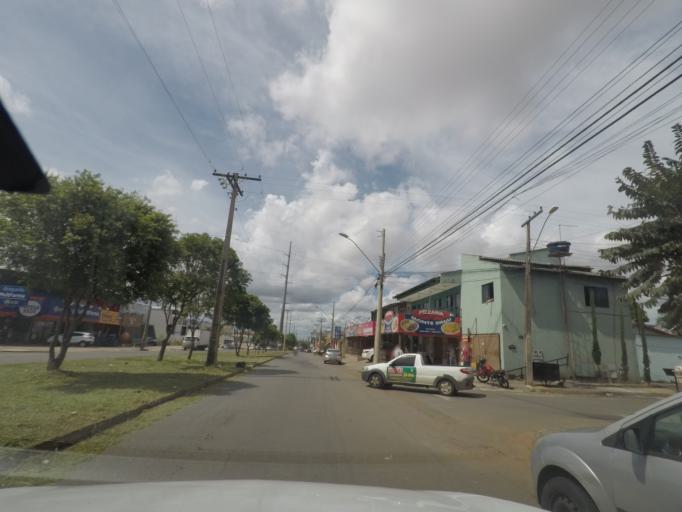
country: BR
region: Goias
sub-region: Goiania
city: Goiania
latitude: -16.7316
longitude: -49.3412
